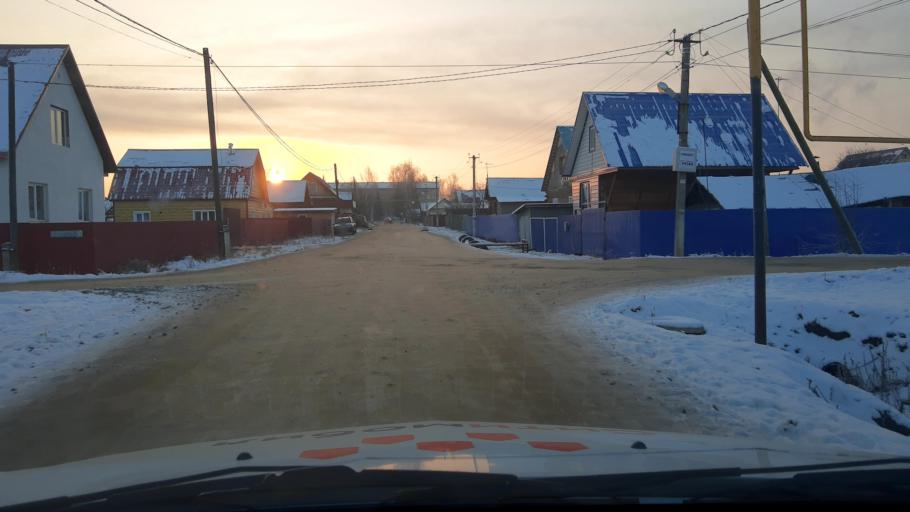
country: RU
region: Bashkortostan
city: Iglino
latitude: 54.8338
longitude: 56.4047
